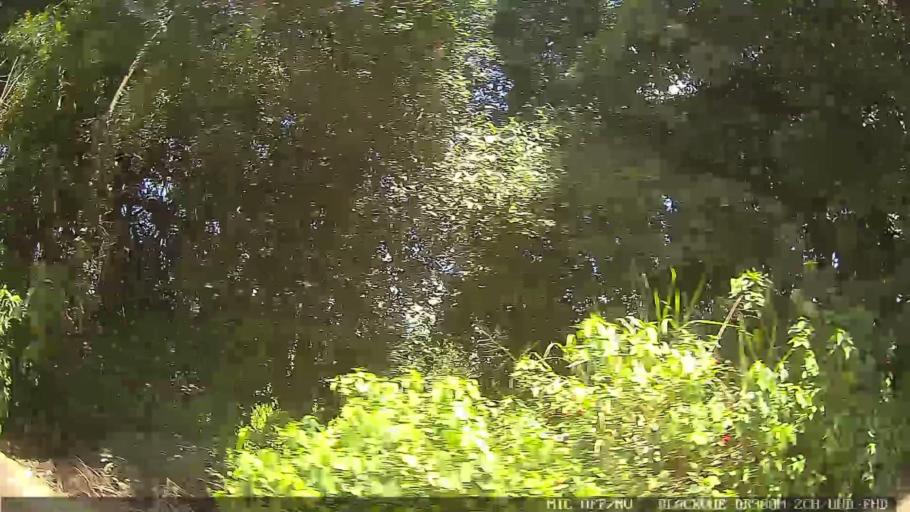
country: BR
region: Sao Paulo
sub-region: Atibaia
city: Atibaia
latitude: -23.1314
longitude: -46.6002
